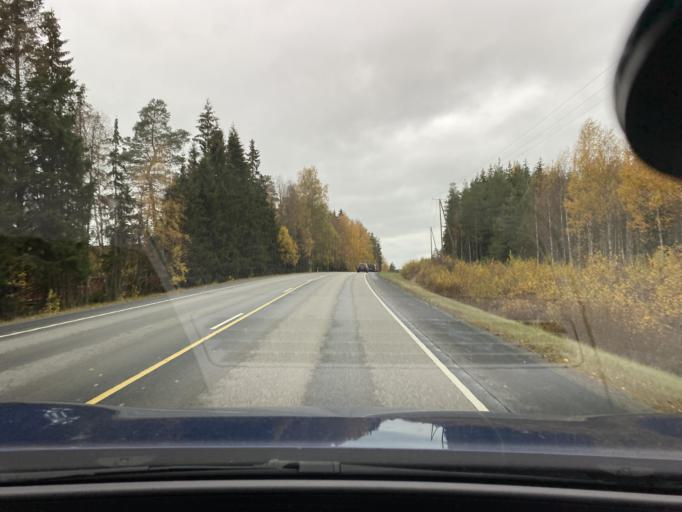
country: FI
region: Satakunta
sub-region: Rauma
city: Lappi
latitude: 61.1028
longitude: 21.8972
